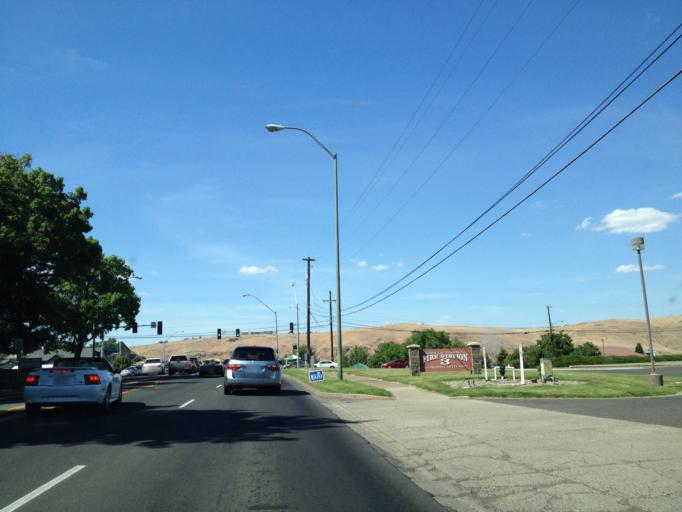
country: US
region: Washington
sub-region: Yakima County
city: West Valley
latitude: 46.6059
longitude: -120.5619
